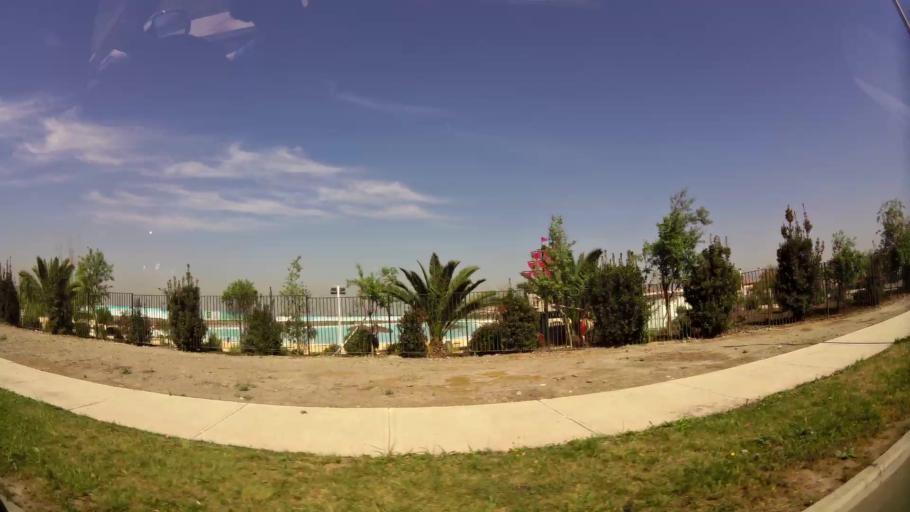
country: CL
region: Santiago Metropolitan
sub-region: Provincia de Talagante
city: Penaflor
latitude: -33.5608
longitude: -70.8293
